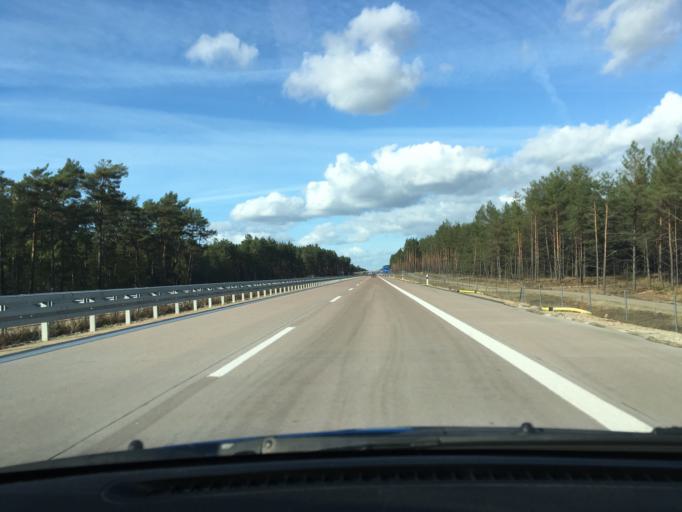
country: DE
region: Mecklenburg-Vorpommern
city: Grabow
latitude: 53.2862
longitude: 11.5269
